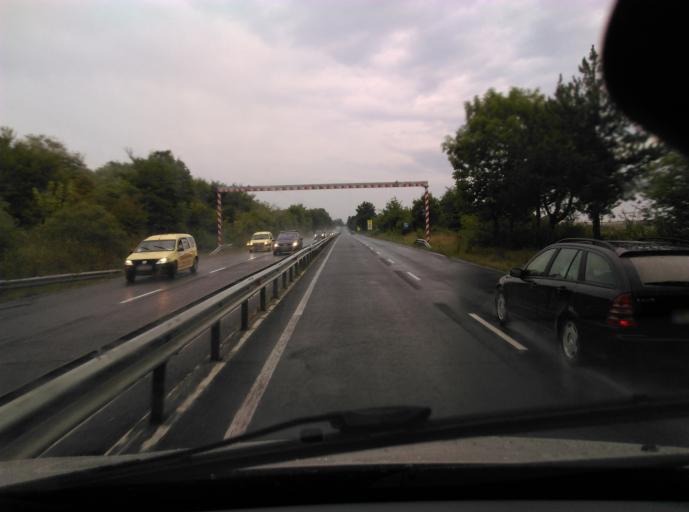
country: BG
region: Burgas
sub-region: Obshtina Burgas
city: Burgas
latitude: 42.4403
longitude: 27.4782
